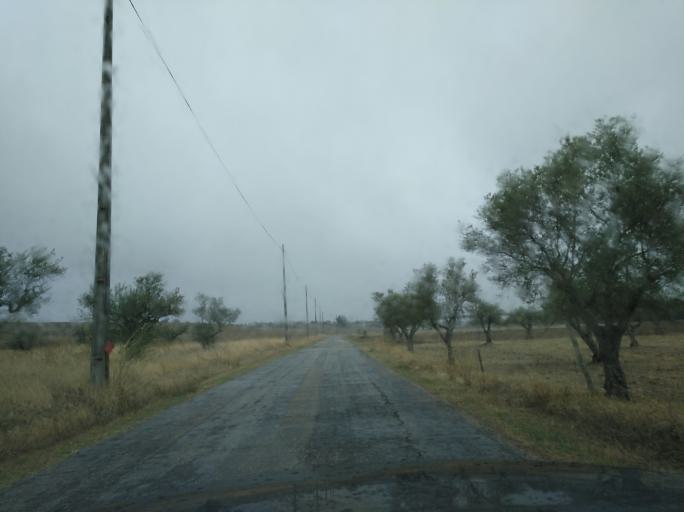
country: PT
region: Portalegre
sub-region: Campo Maior
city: Campo Maior
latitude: 38.9766
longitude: -7.0691
